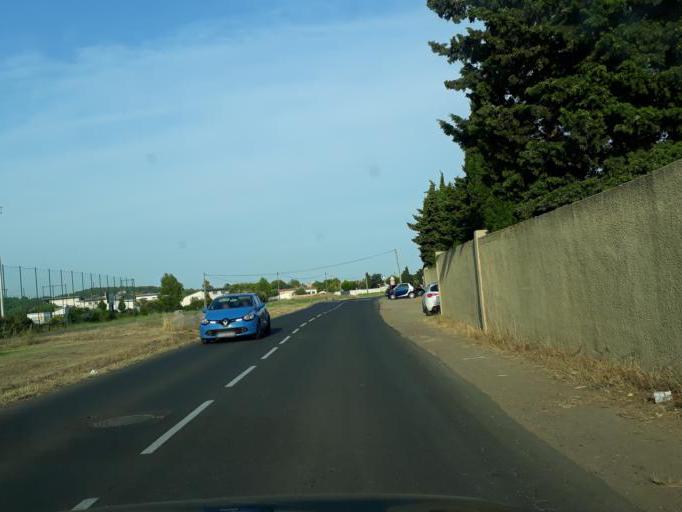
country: FR
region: Languedoc-Roussillon
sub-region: Departement de l'Herault
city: Agde
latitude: 43.2871
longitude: 3.4771
